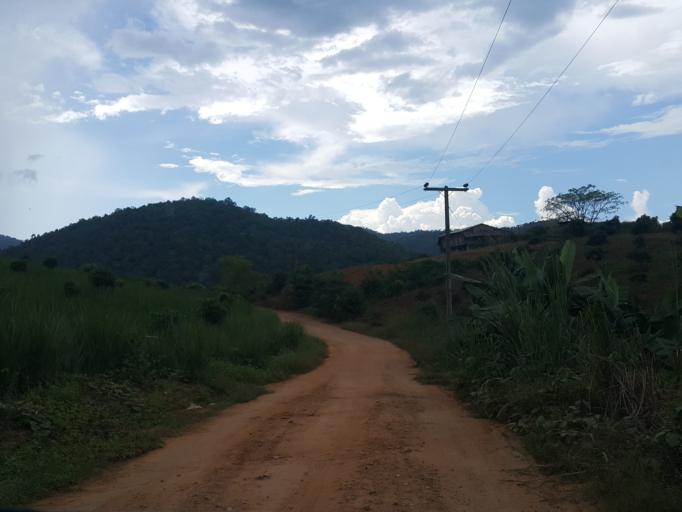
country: TH
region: Chiang Mai
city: Phrao
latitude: 19.3293
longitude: 99.1370
